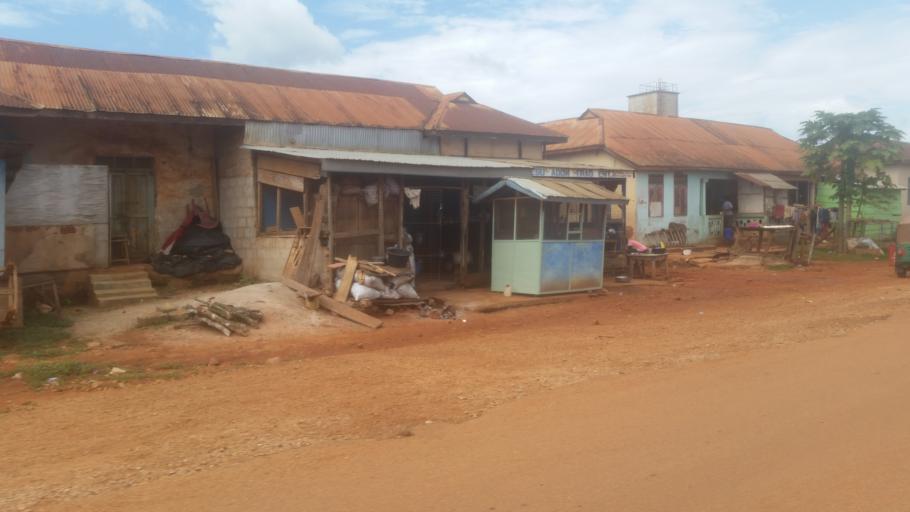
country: GH
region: Western
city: Bibiani
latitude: 6.8044
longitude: -2.5215
